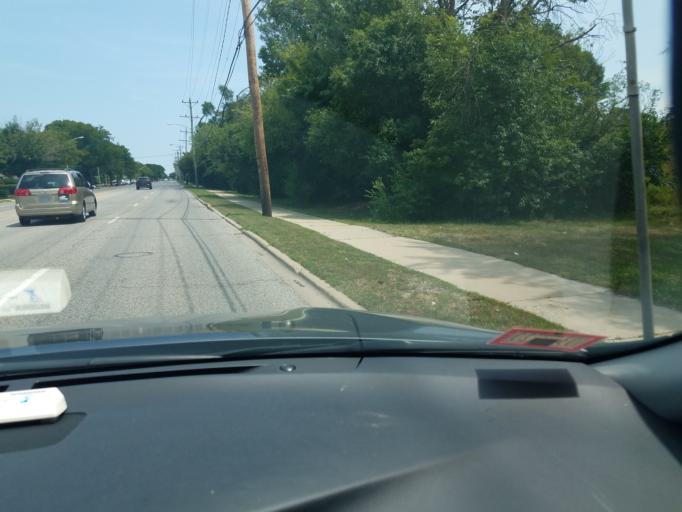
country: US
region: Illinois
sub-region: Cook County
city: Skokie
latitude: 42.0407
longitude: -87.7436
